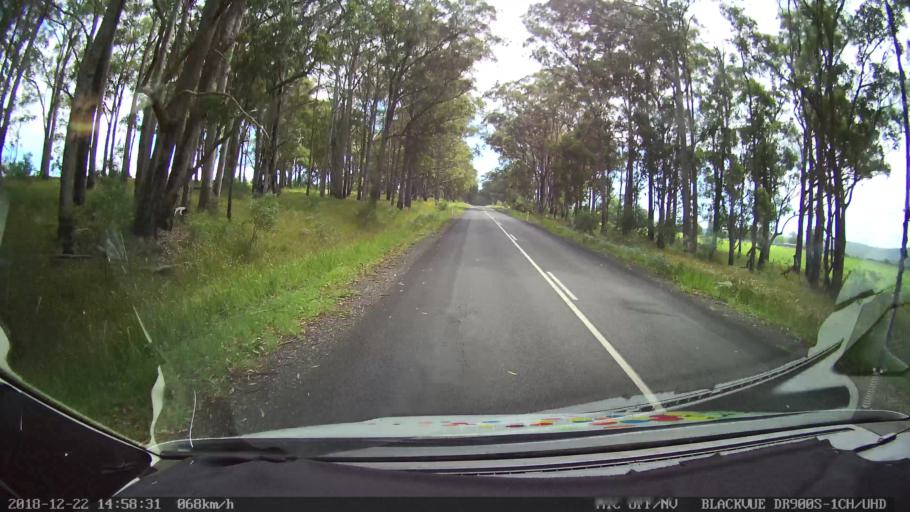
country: AU
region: New South Wales
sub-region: Bellingen
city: Dorrigo
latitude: -30.2406
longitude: 152.4903
